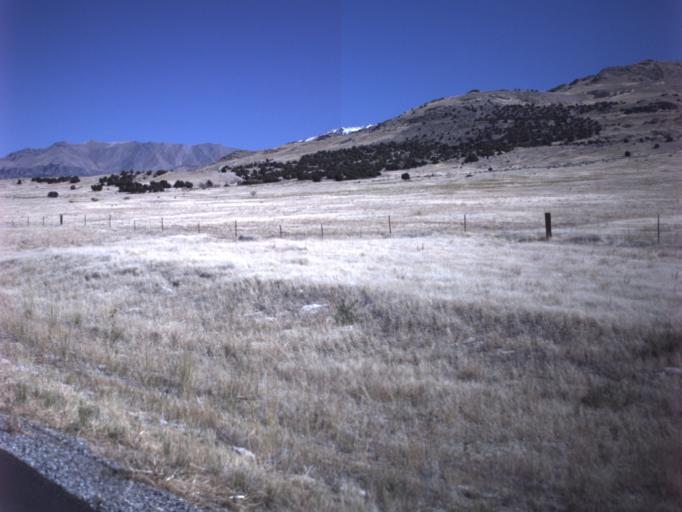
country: US
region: Utah
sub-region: Tooele County
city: Grantsville
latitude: 40.5674
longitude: -112.7321
